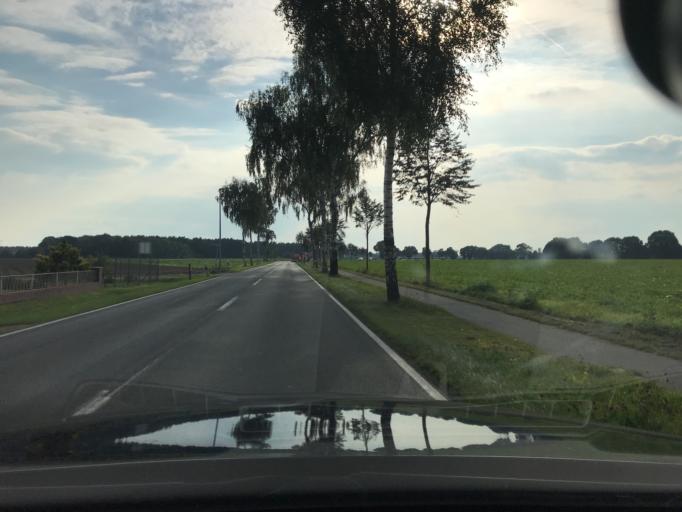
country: DE
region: Lower Saxony
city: Syke
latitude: 52.9681
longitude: 8.8626
